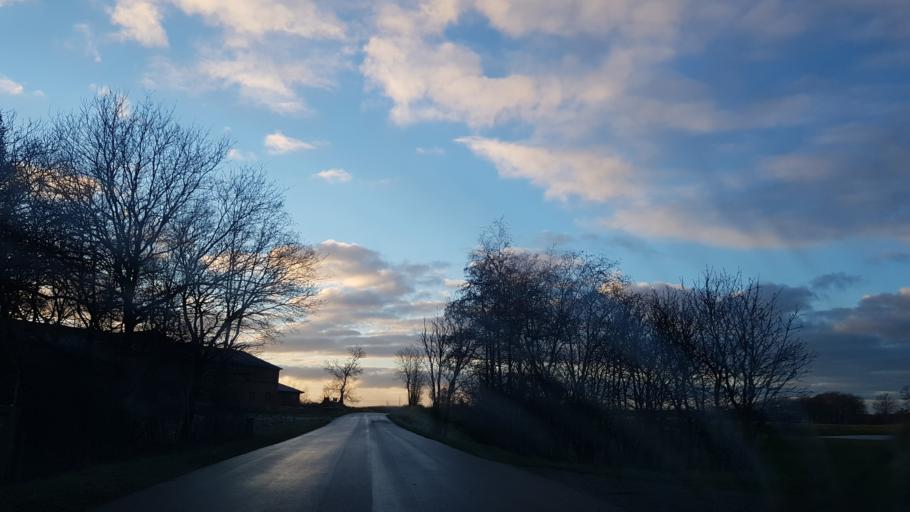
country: DK
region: South Denmark
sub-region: Kolding Kommune
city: Vamdrup
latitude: 55.3743
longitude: 9.2967
